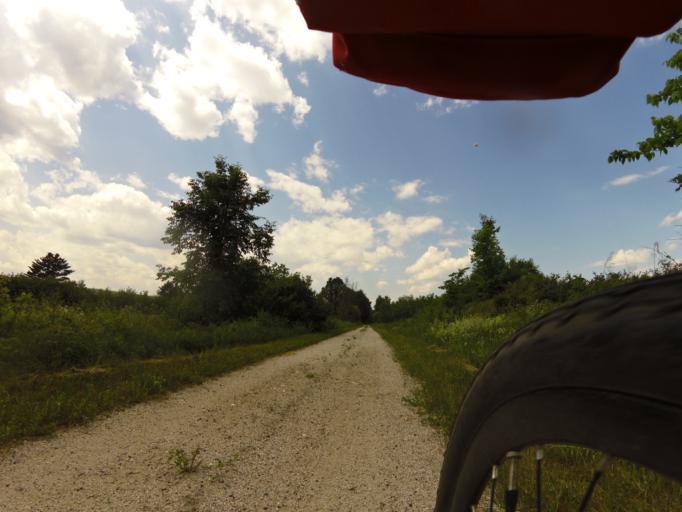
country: CA
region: Quebec
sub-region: Outaouais
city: Maniwaki
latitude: 46.0591
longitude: -76.1077
